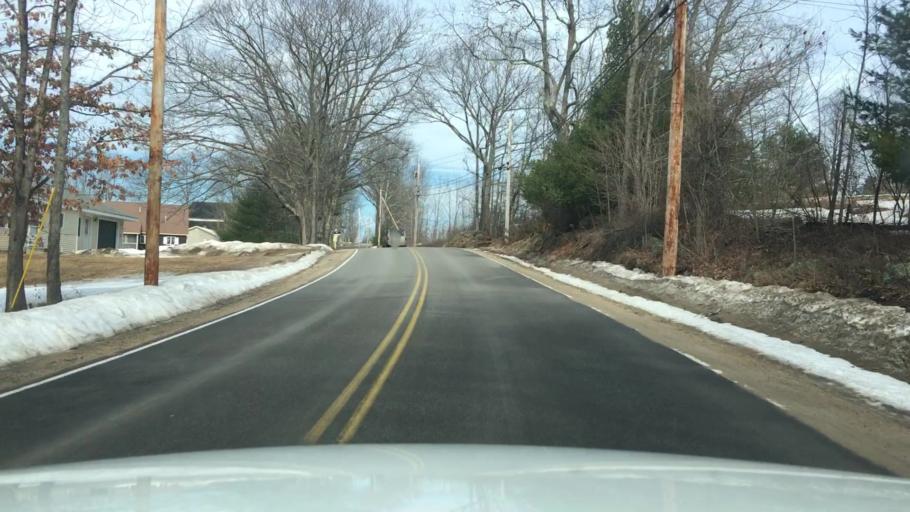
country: US
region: Maine
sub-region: York County
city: Springvale
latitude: 43.4899
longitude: -70.8072
